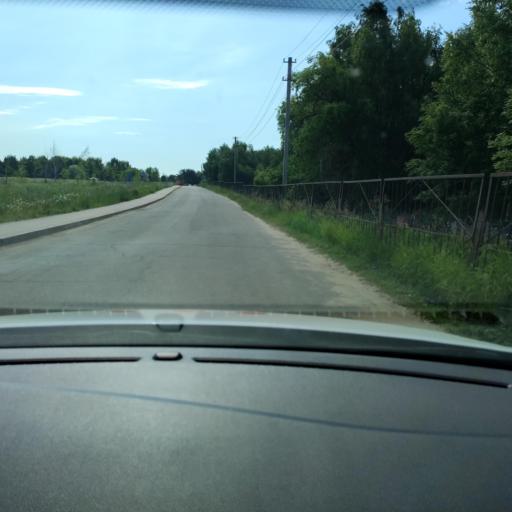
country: RU
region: Tatarstan
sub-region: Gorod Kazan'
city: Kazan
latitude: 55.8905
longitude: 49.0938
